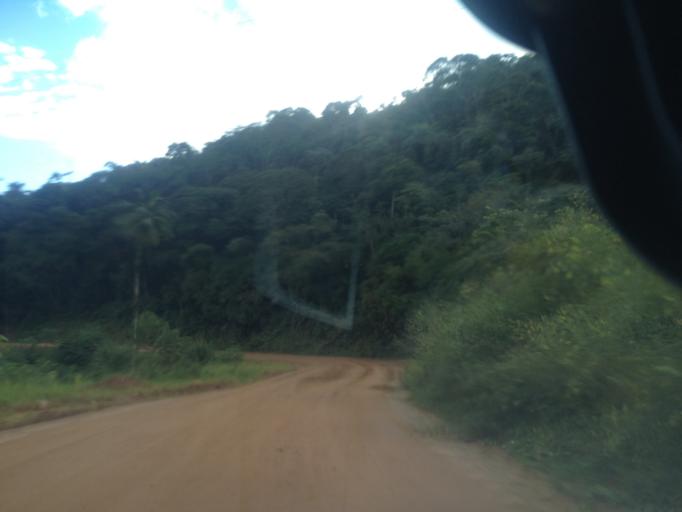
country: BR
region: Rio de Janeiro
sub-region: Quatis
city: Quatis
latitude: -22.2321
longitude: -44.2577
